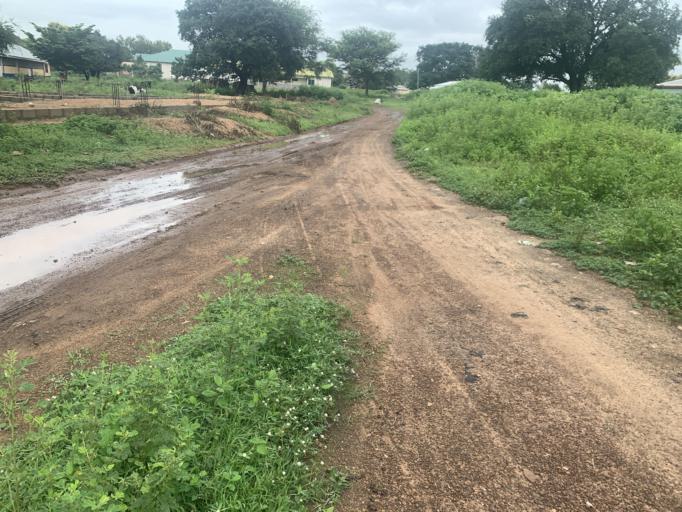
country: GH
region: Upper East
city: Navrongo
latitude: 10.8659
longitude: -1.0806
